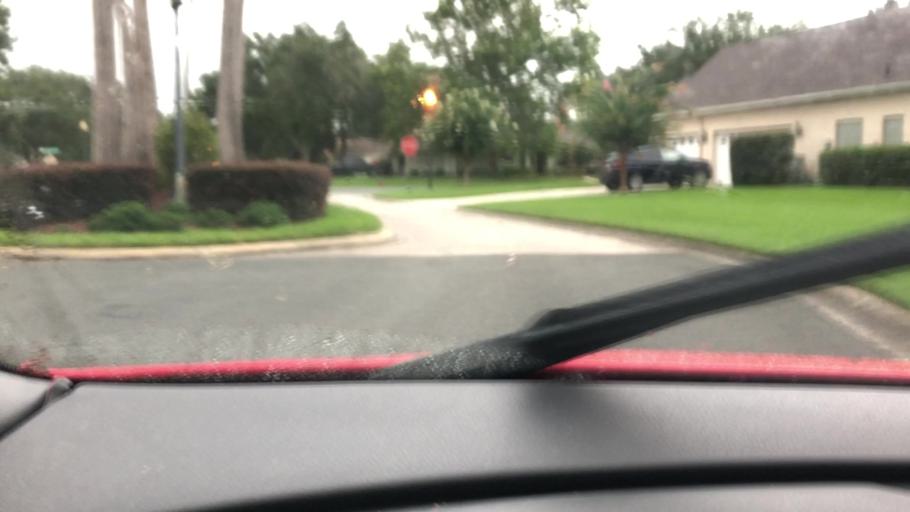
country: US
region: Florida
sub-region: Lake County
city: Mount Dora
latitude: 28.8477
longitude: -81.6380
